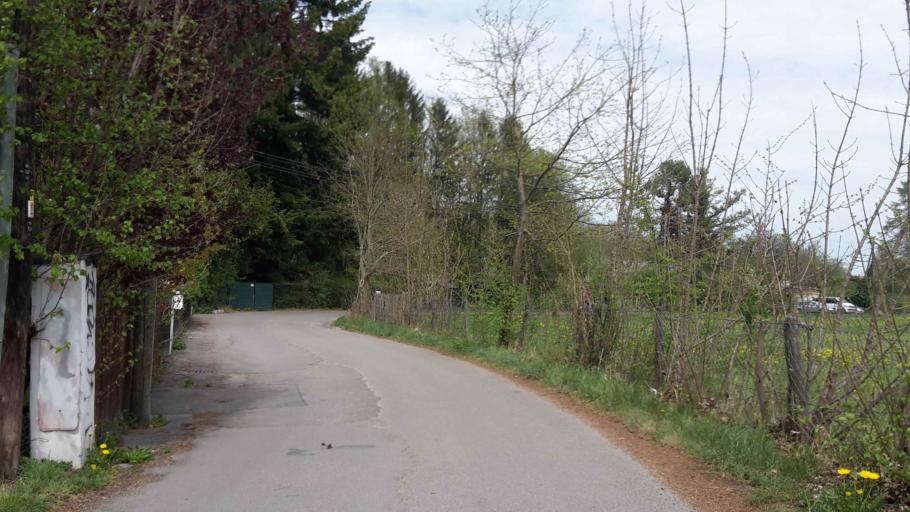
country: DE
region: Bavaria
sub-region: Upper Bavaria
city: Karlsfeld
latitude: 48.1893
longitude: 11.4904
